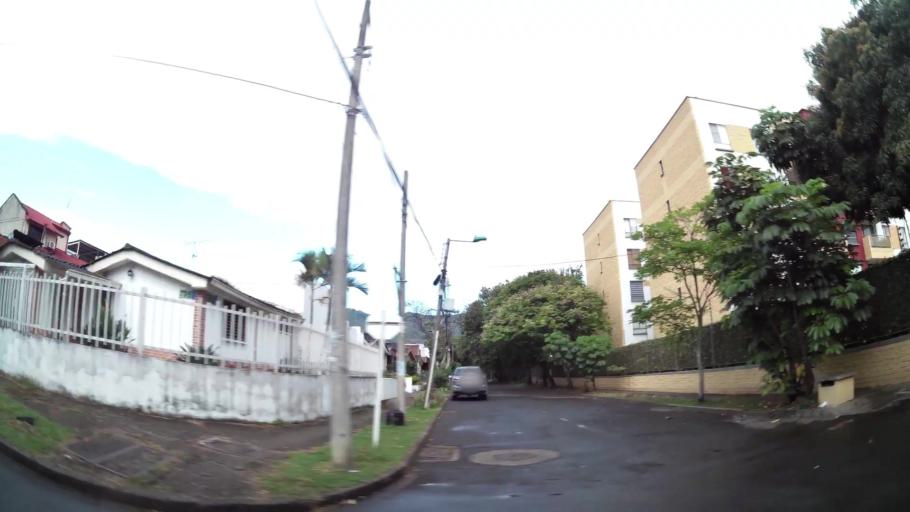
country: CO
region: Valle del Cauca
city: Cali
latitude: 3.4777
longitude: -76.5197
